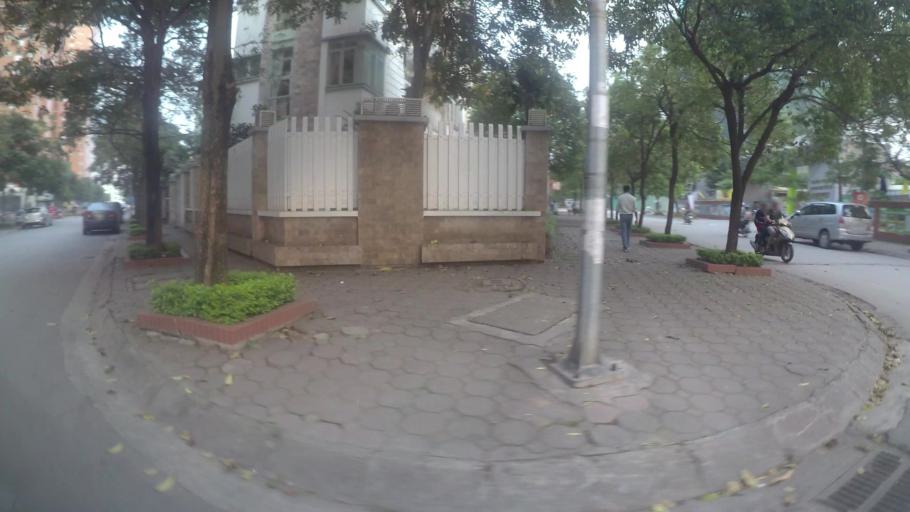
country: VN
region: Ha Noi
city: Cau Giay
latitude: 21.0511
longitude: 105.7928
